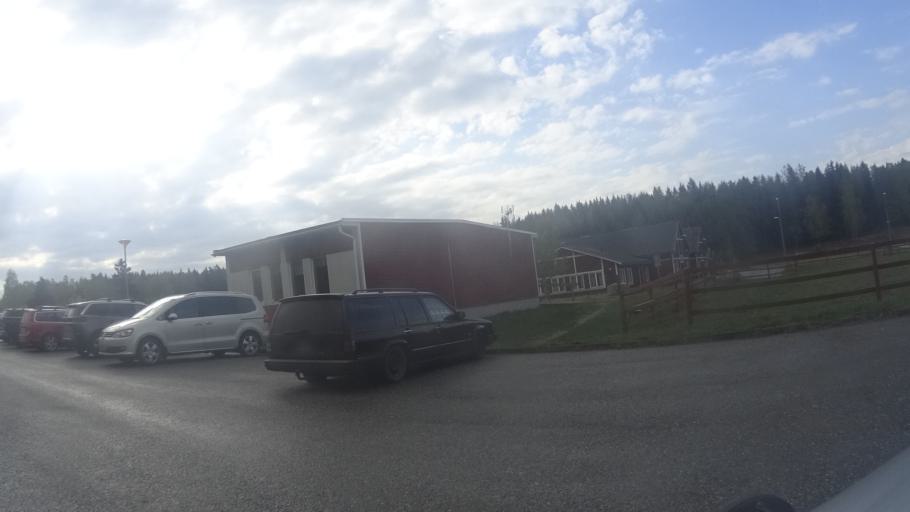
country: SE
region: OErebro
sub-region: Orebro Kommun
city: Hovsta
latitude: 59.3557
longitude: 15.2405
